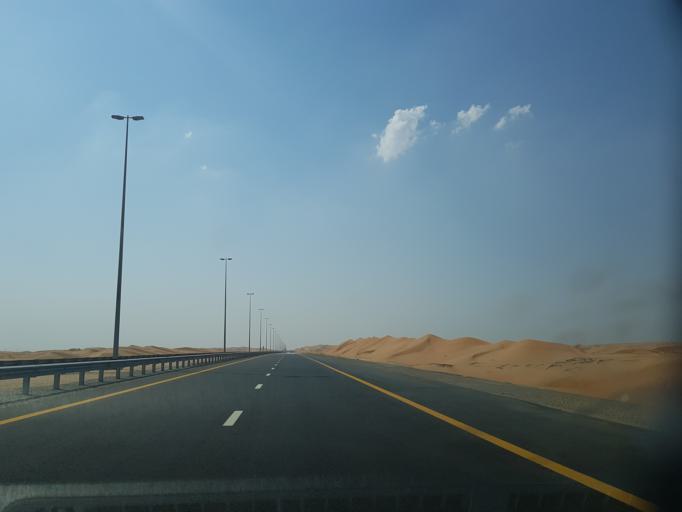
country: AE
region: Ash Shariqah
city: Adh Dhayd
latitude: 25.2569
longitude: 55.7206
